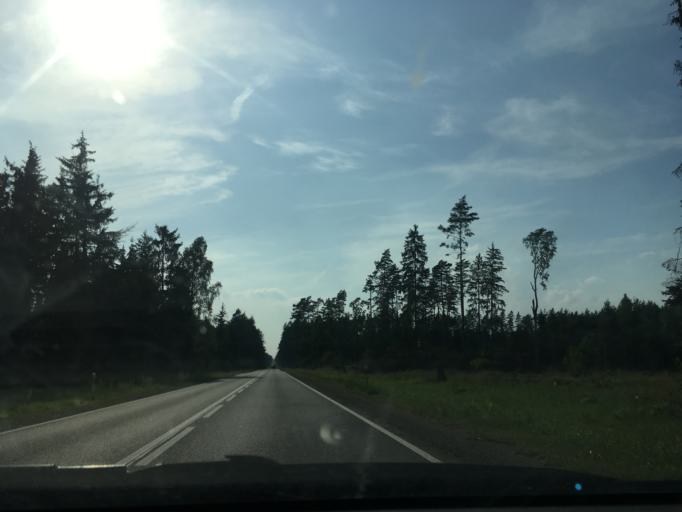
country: PL
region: Podlasie
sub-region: Powiat bialostocki
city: Suprasl
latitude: 53.1256
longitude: 23.3552
